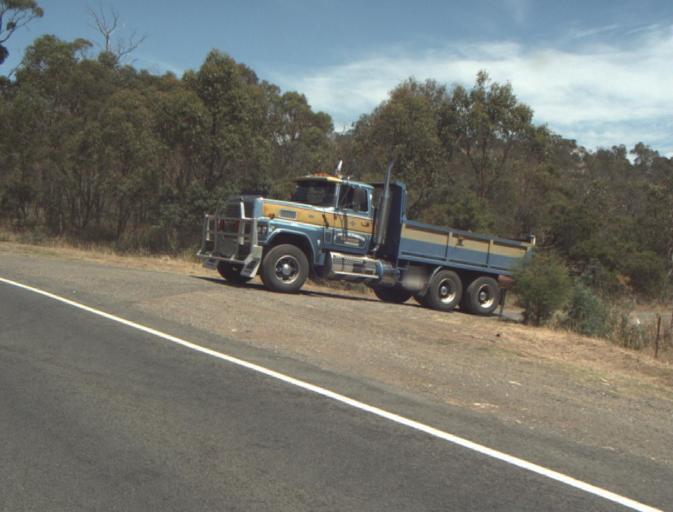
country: AU
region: Tasmania
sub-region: Launceston
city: Mayfield
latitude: -41.3448
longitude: 147.1407
